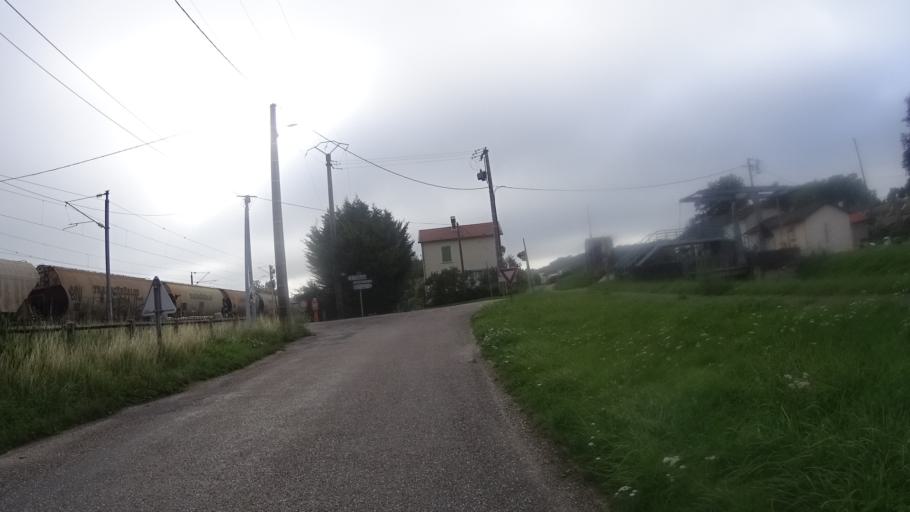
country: FR
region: Lorraine
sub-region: Departement de la Meuse
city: Fains-Veel
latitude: 48.8039
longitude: 5.0700
